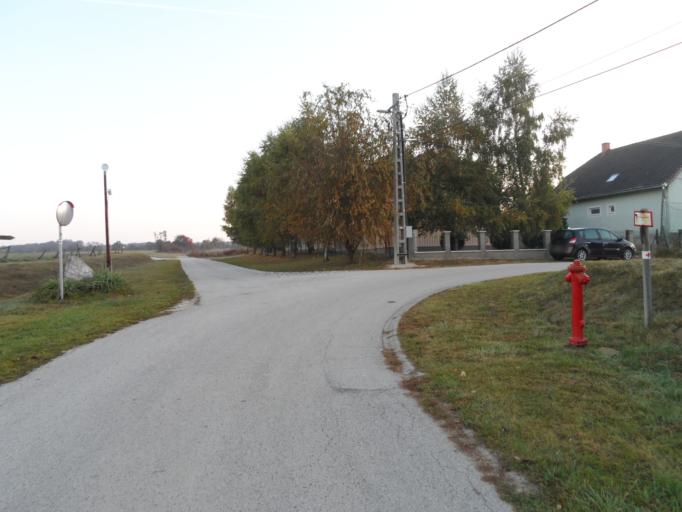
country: HU
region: Veszprem
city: Herend
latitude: 47.1833
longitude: 17.6868
